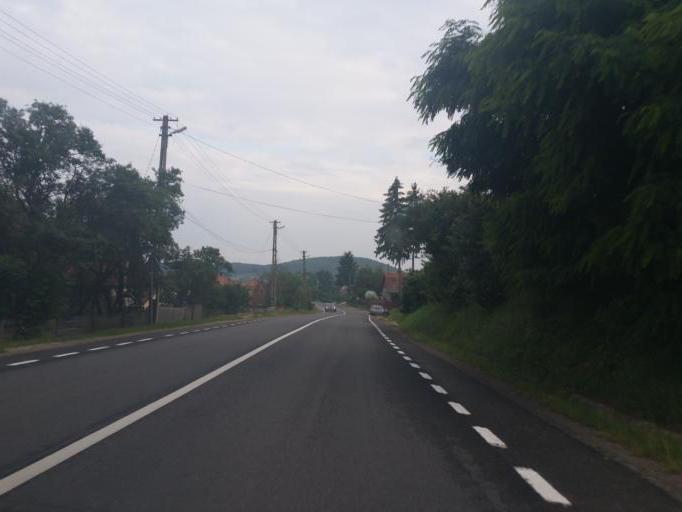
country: RO
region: Cluj
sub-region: Comuna Sanpaul
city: Sanpaul
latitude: 46.9073
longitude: 23.4170
